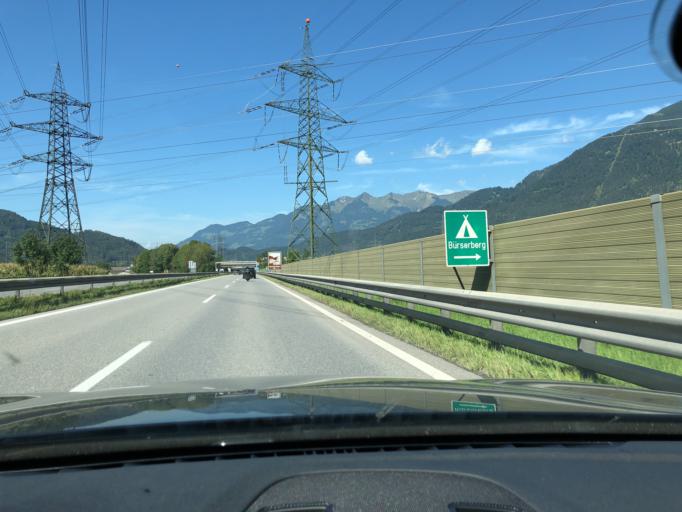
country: AT
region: Vorarlberg
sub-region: Politischer Bezirk Bludenz
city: Bludenz
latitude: 47.1422
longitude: 9.8236
